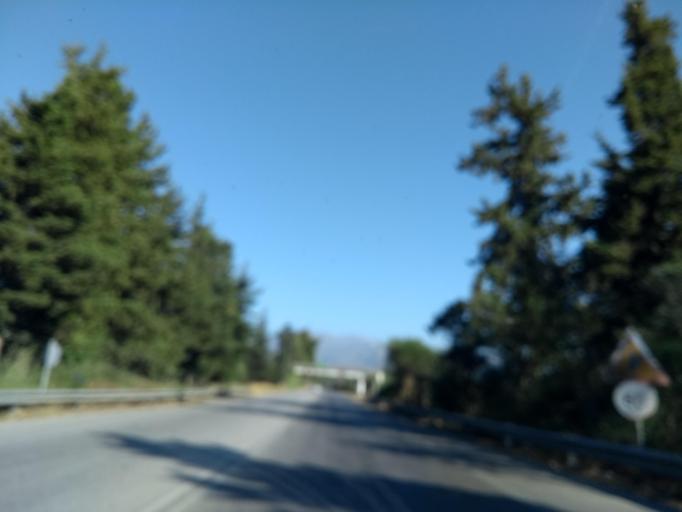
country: GR
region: Crete
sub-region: Nomos Chanias
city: Kalivai
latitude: 35.4023
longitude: 24.1512
